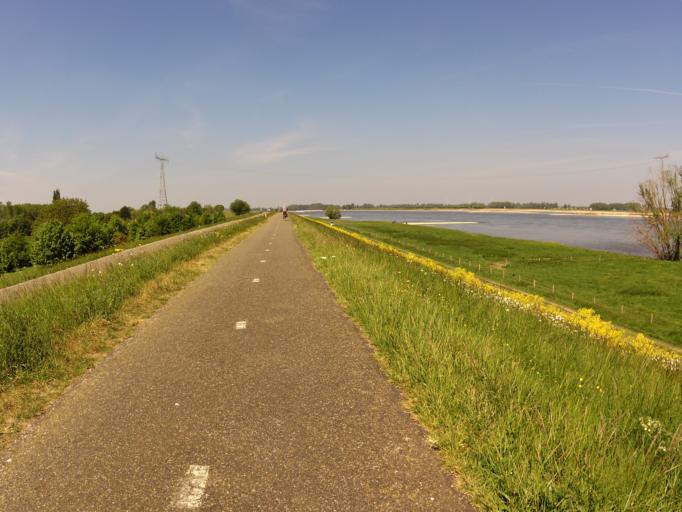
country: NL
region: Gelderland
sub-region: Gemeente Neerijnen
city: Neerijnen
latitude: 51.8057
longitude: 5.3341
